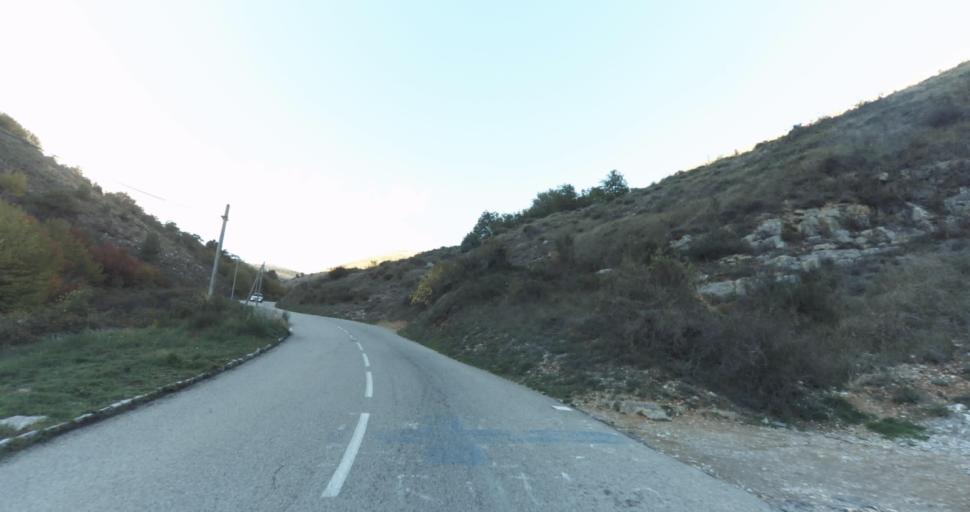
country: FR
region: Provence-Alpes-Cote d'Azur
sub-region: Departement des Alpes-Maritimes
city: Vence
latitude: 43.7437
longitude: 7.1038
